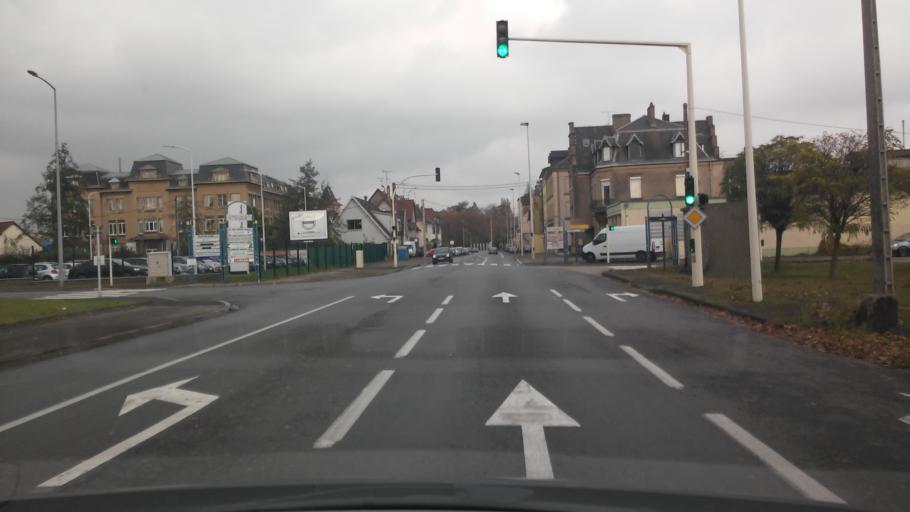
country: FR
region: Lorraine
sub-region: Departement de la Moselle
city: Terville
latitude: 49.3421
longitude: 6.1607
